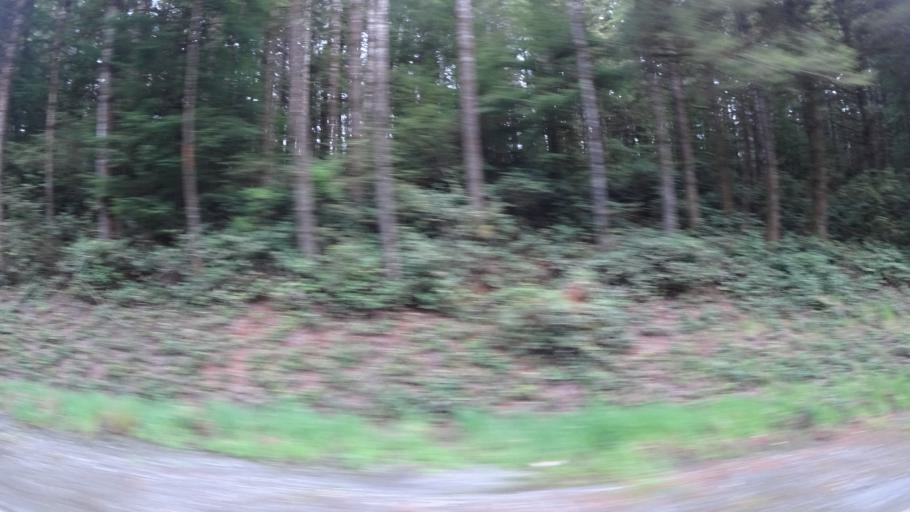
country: US
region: Oregon
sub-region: Coos County
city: Coquille
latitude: 43.2274
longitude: -124.2980
